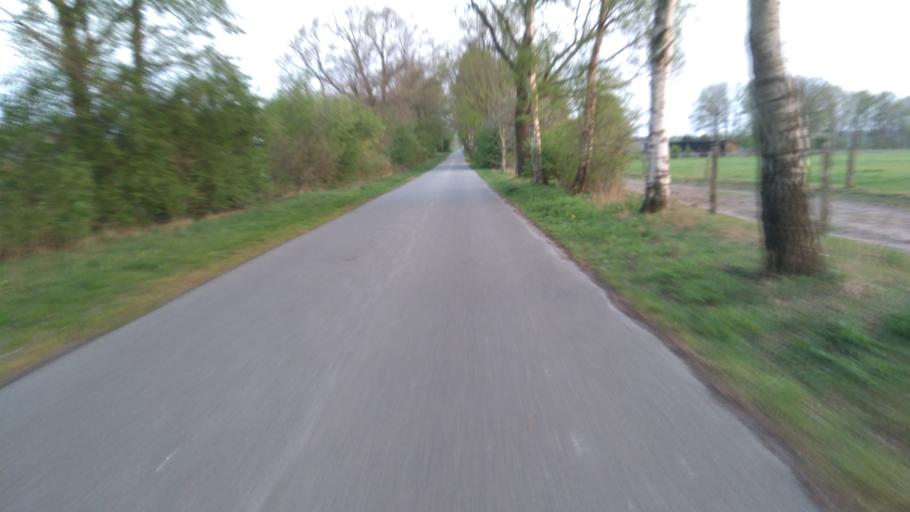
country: DE
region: Lower Saxony
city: Bargstedt
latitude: 53.4831
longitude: 9.4781
